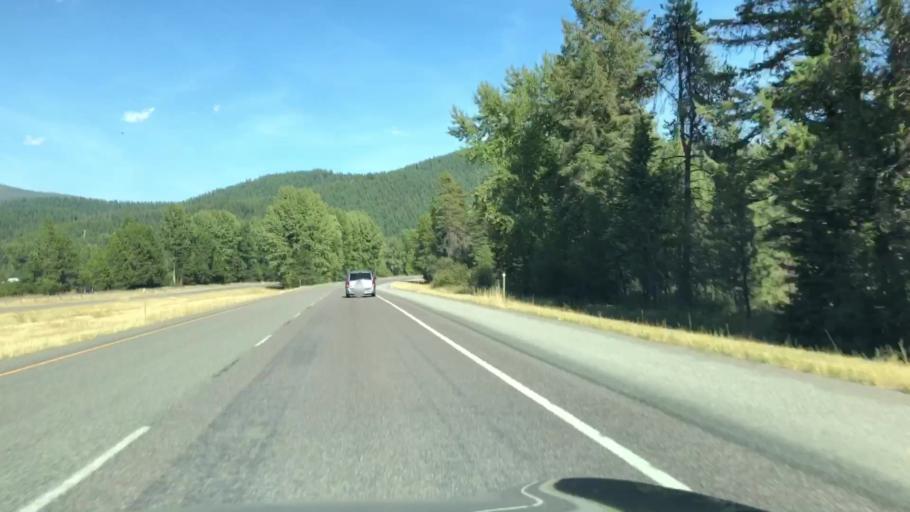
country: US
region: Montana
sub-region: Sanders County
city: Thompson Falls
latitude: 47.3780
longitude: -115.3628
